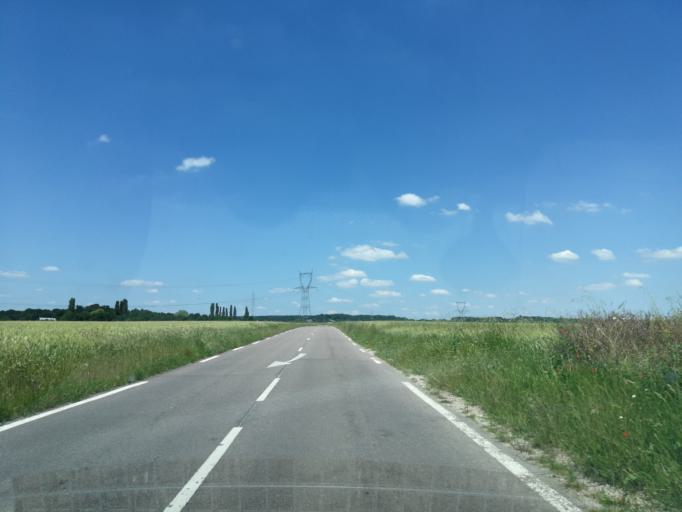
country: FR
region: Ile-de-France
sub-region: Departement de l'Essonne
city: Vaugrigneuse
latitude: 48.6070
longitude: 2.1250
